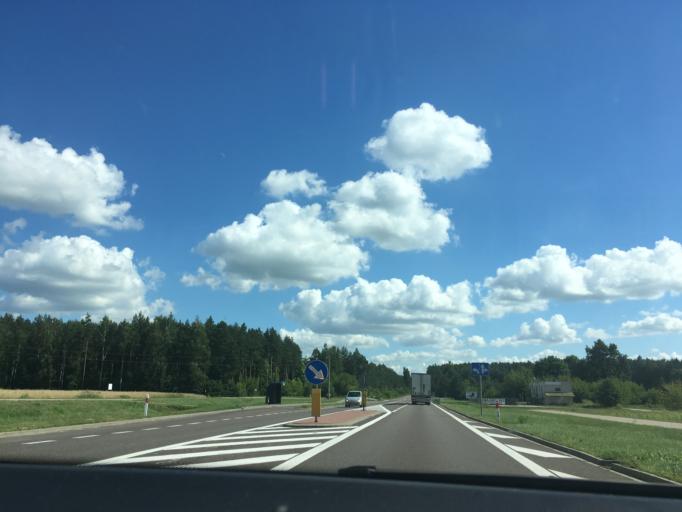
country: PL
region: Podlasie
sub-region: Powiat augustowski
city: Augustow
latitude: 53.7388
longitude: 23.0984
